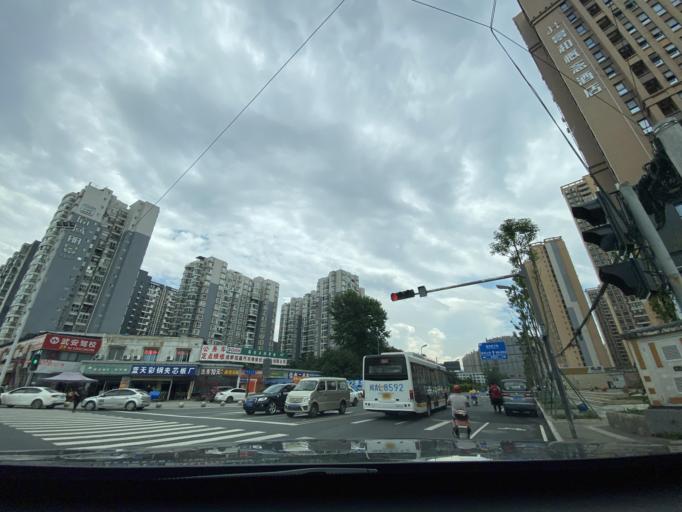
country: CN
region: Sichuan
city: Dongsheng
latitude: 30.5137
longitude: 104.0390
